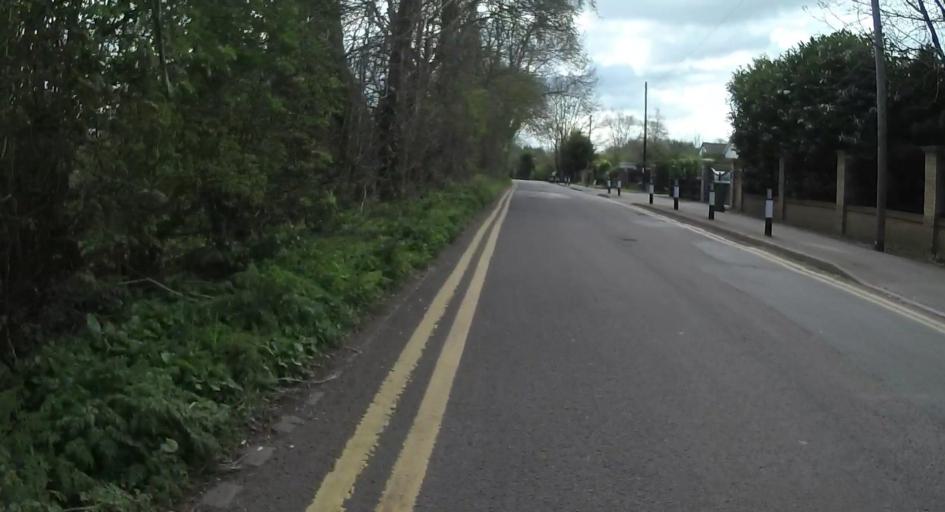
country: GB
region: England
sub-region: Surrey
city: Shepperton
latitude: 51.3854
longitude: -0.4582
